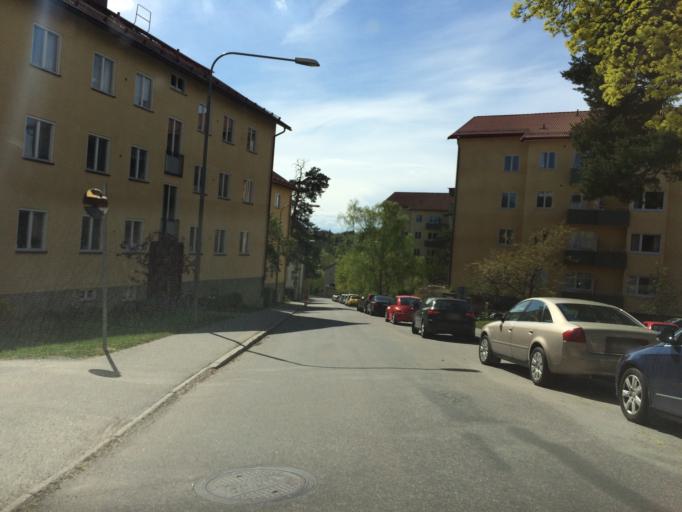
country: SE
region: Stockholm
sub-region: Stockholms Kommun
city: Bromma
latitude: 59.3050
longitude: 17.9628
